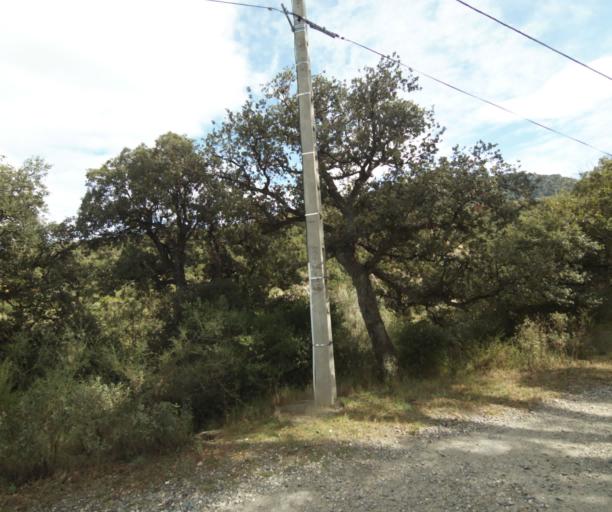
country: FR
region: Languedoc-Roussillon
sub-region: Departement des Pyrenees-Orientales
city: Sant Andreu de Sureda
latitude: 42.5269
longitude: 2.9864
